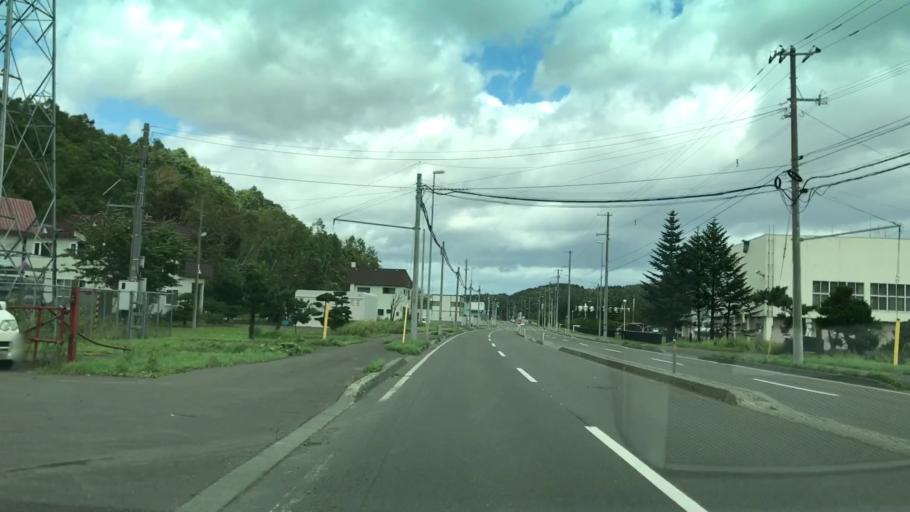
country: JP
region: Hokkaido
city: Kitahiroshima
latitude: 42.9702
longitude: 141.4528
